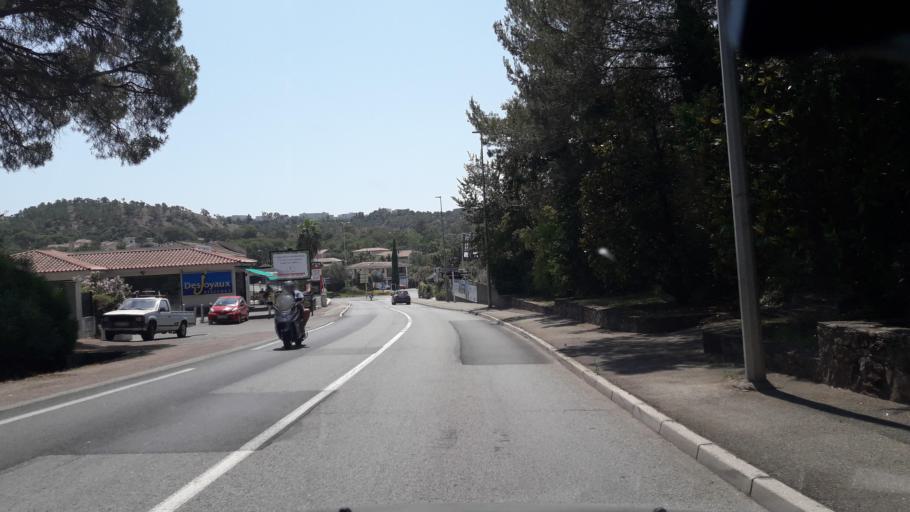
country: FR
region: Provence-Alpes-Cote d'Azur
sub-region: Departement du Var
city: Saint-Raphael
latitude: 43.4393
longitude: 6.7833
